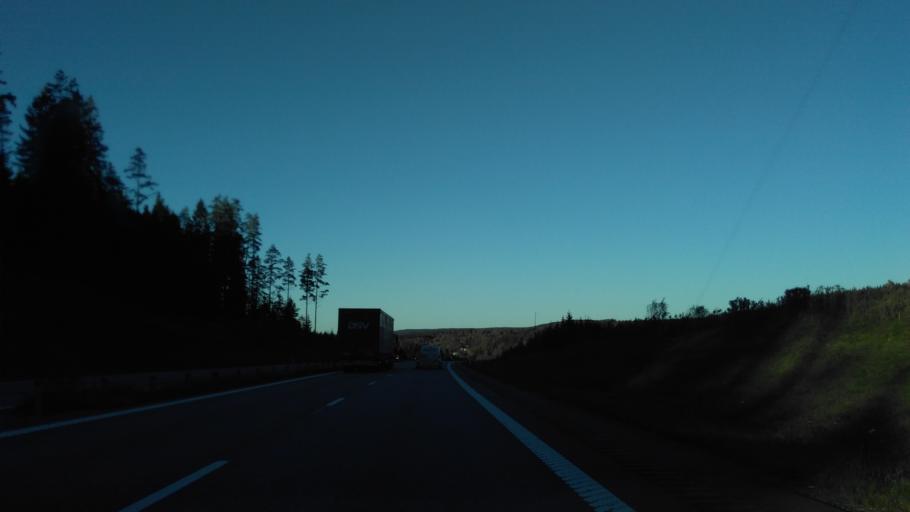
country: SE
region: Vaestra Goetaland
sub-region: Boras Kommun
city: Dalsjofors
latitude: 57.7803
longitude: 13.1191
